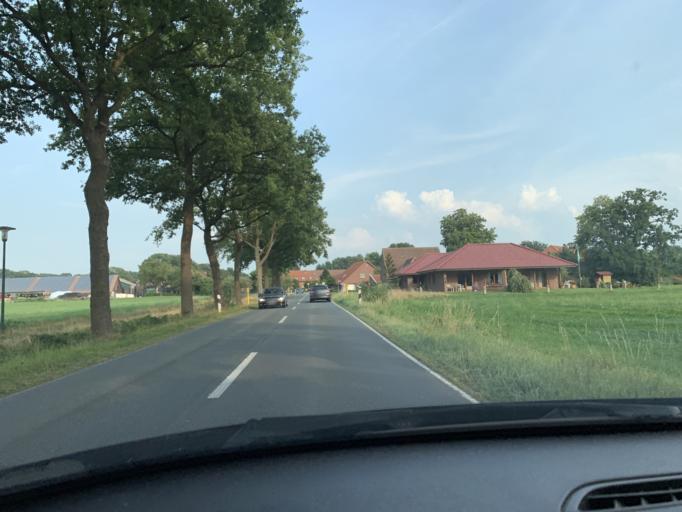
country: DE
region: Lower Saxony
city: Barssel
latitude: 53.1756
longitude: 7.7706
